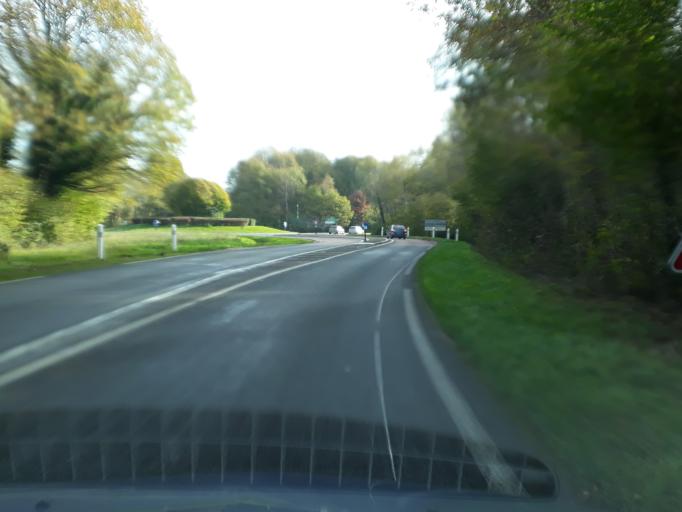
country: FR
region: Ile-de-France
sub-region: Departement de Seine-et-Marne
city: La Grande-Paroisse
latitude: 48.4183
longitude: 2.9136
